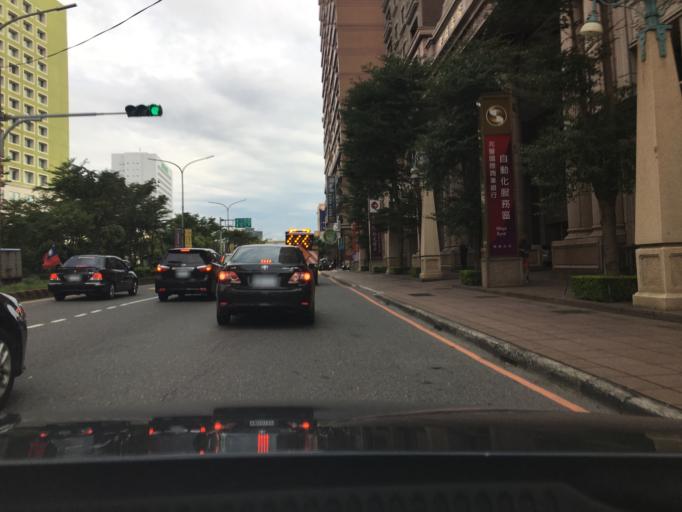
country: TW
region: Taiwan
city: Taoyuan City
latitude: 25.0429
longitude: 121.2946
